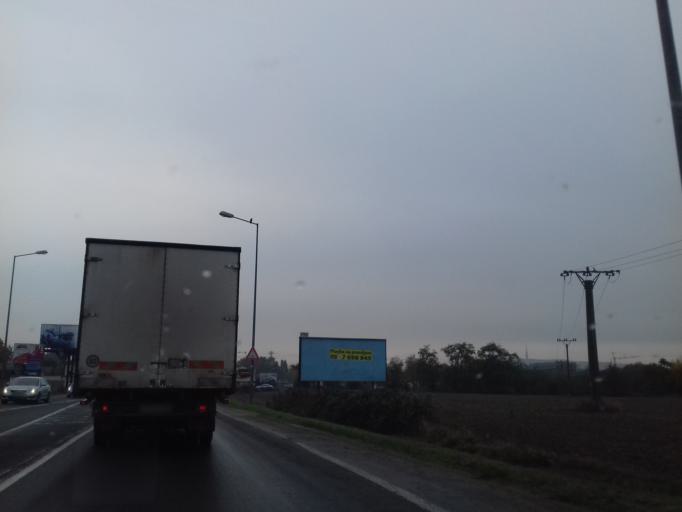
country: SK
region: Bratislavsky
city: Bratislava
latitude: 48.1356
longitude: 17.1599
